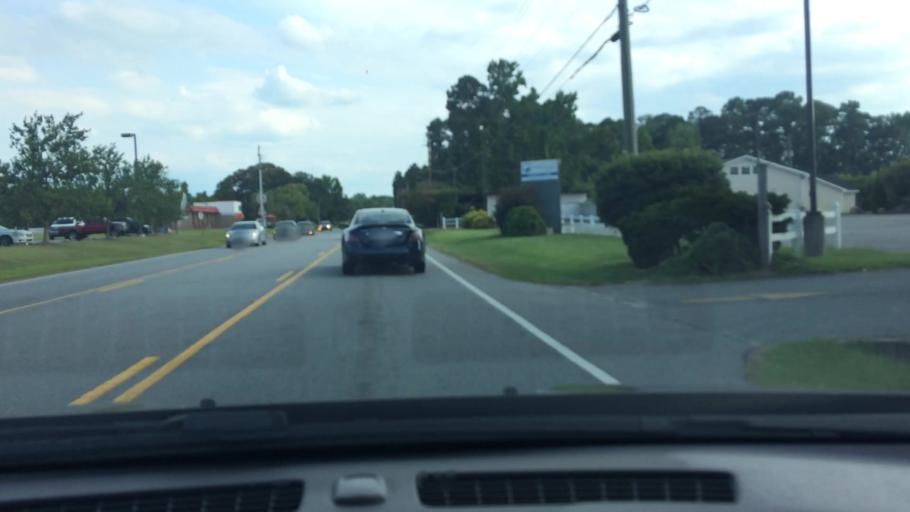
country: US
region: North Carolina
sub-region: Pitt County
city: Windsor
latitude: 35.5502
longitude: -77.3843
